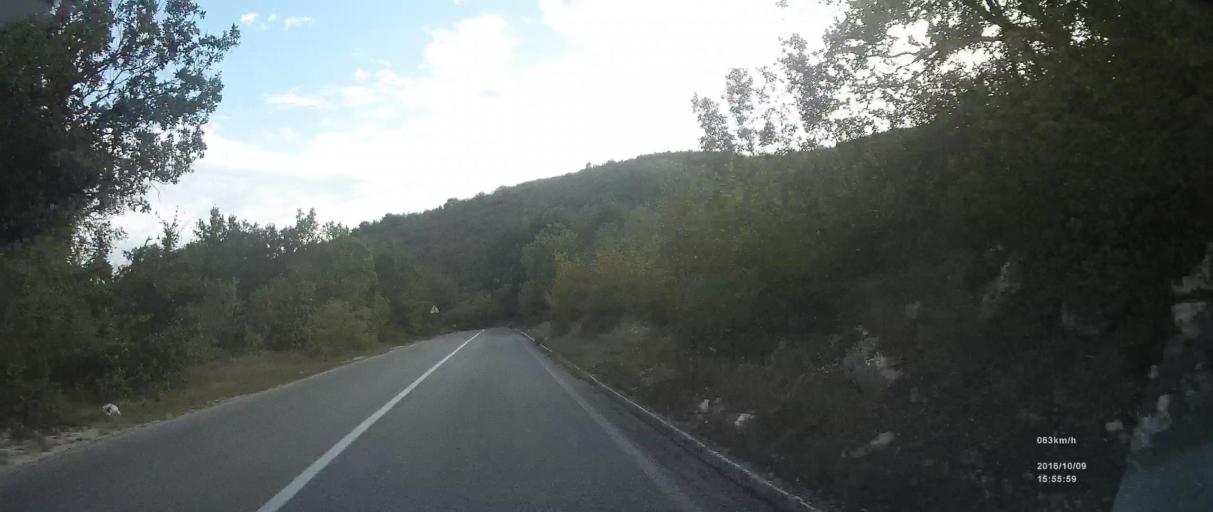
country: HR
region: Splitsko-Dalmatinska
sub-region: Grad Trogir
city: Trogir
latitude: 43.5819
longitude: 16.2321
